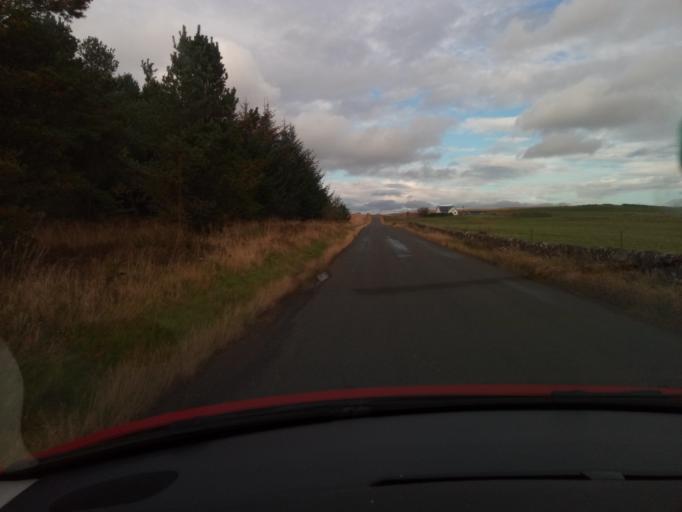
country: GB
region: Scotland
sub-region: South Lanarkshire
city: Carnwath
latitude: 55.7186
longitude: -3.6002
